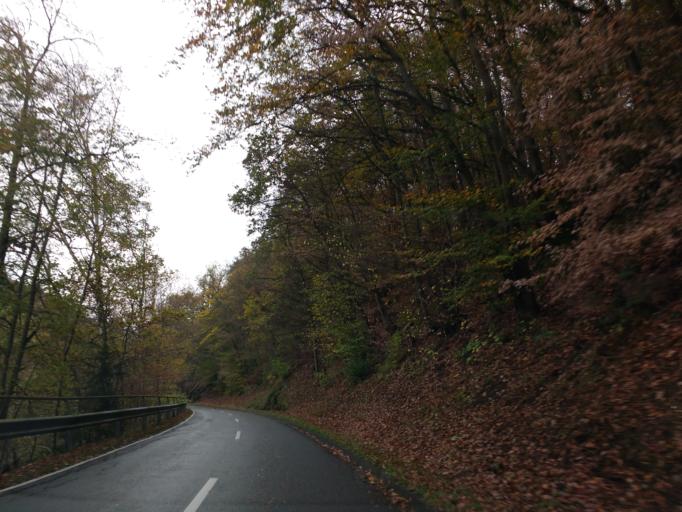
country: DE
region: Hesse
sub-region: Regierungsbezirk Kassel
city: Sachsenhausen
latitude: 51.2047
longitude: 9.0009
